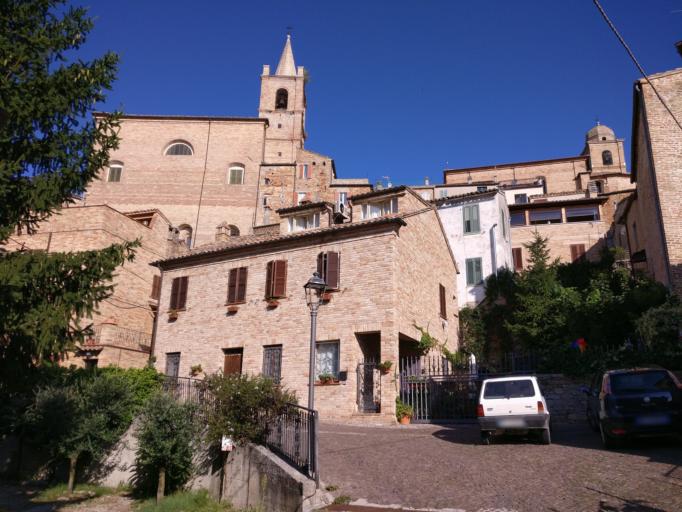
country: IT
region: The Marches
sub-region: Provincia di Ascoli Piceno
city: Montedinove
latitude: 42.9704
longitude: 13.5880
